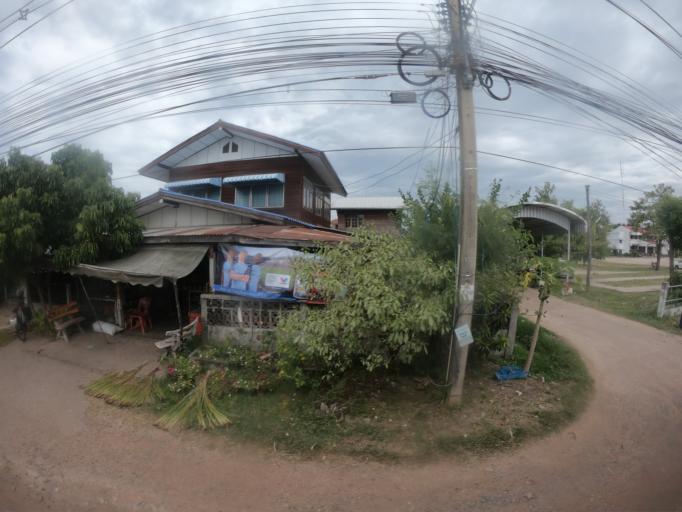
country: TH
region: Maha Sarakham
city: Kantharawichai
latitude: 16.3373
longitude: 103.1920
